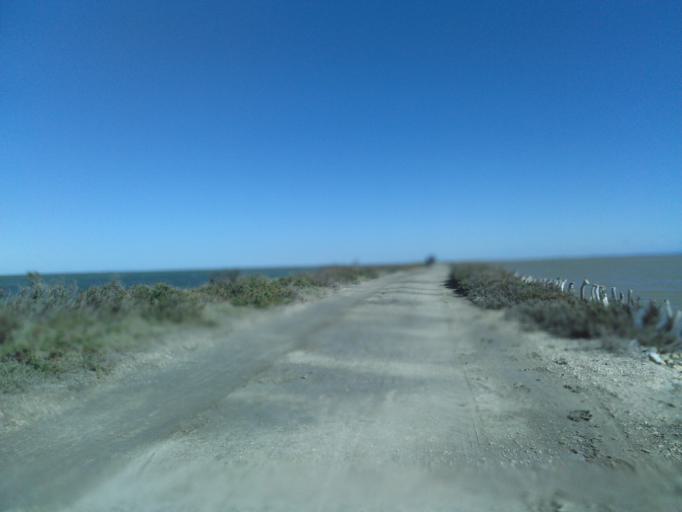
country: FR
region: Provence-Alpes-Cote d'Azur
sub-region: Departement des Bouches-du-Rhone
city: Saintes-Maries-de-la-Mer
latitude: 43.4211
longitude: 4.6187
